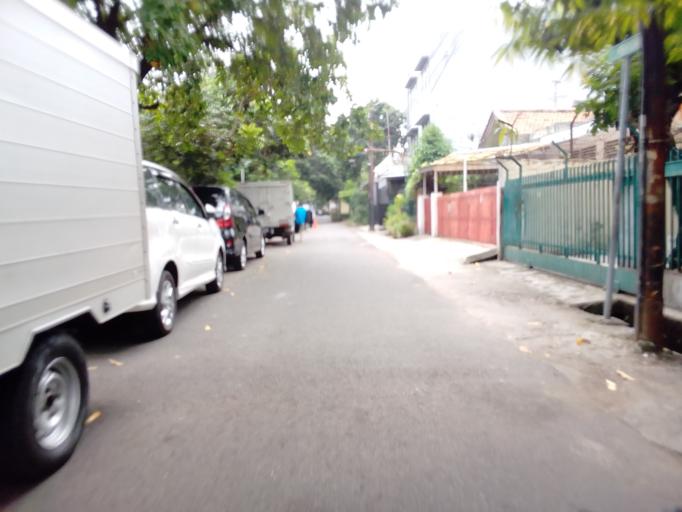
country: ID
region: Jakarta Raya
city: Jakarta
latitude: -6.1621
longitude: 106.8099
